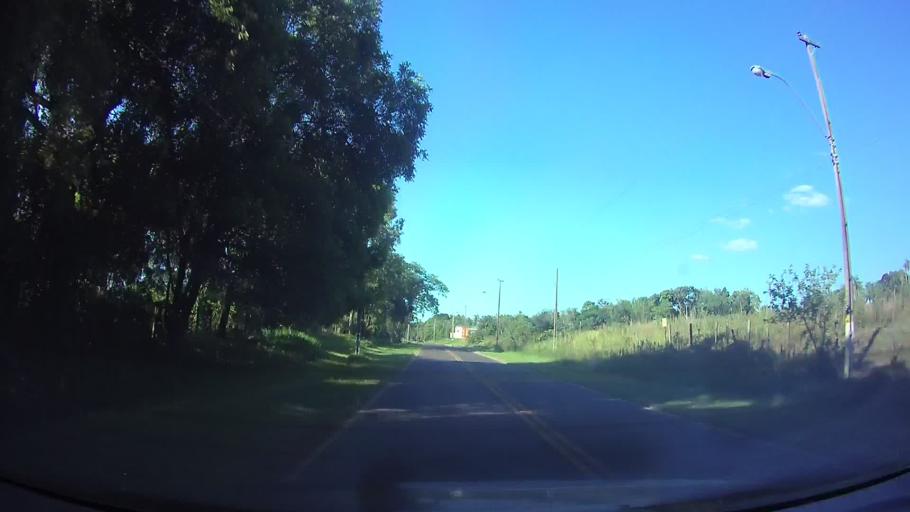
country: PY
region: Cordillera
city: Atyra
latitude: -25.3007
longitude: -57.1854
